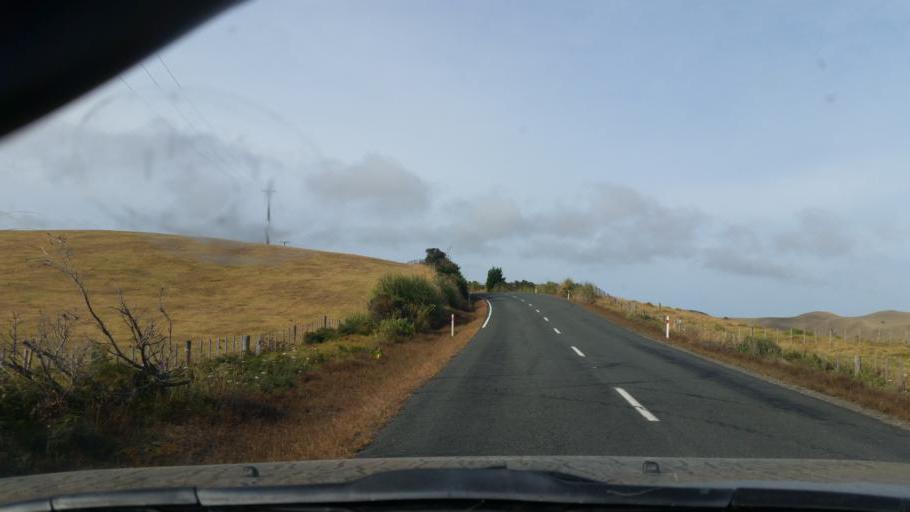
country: NZ
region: Northland
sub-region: Kaipara District
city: Dargaville
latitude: -36.2026
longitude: 174.0460
